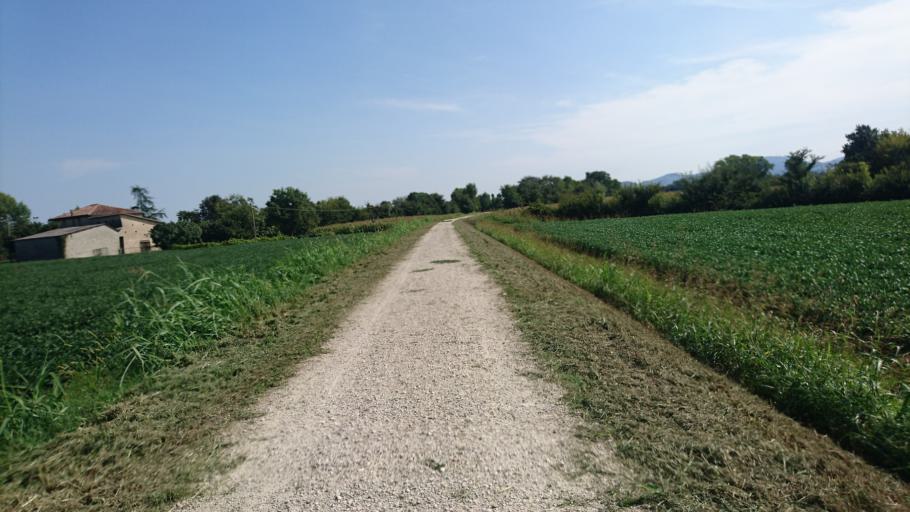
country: IT
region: Veneto
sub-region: Provincia di Padova
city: Veggiano
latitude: 45.4330
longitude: 11.7268
